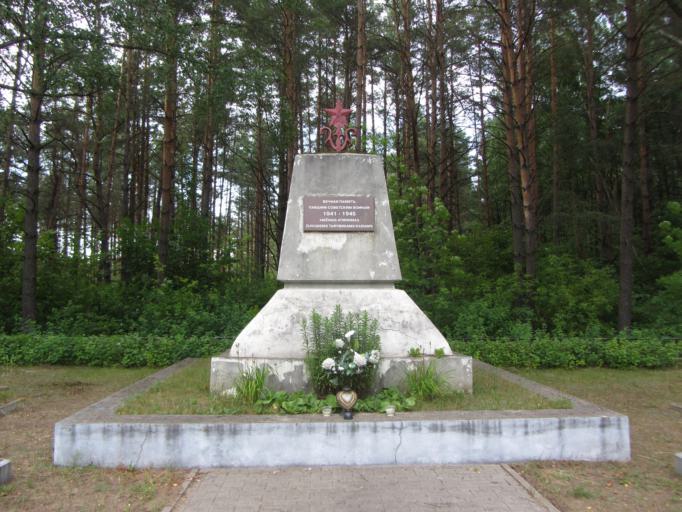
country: LT
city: Veisiejai
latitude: 54.0003
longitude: 23.6678
